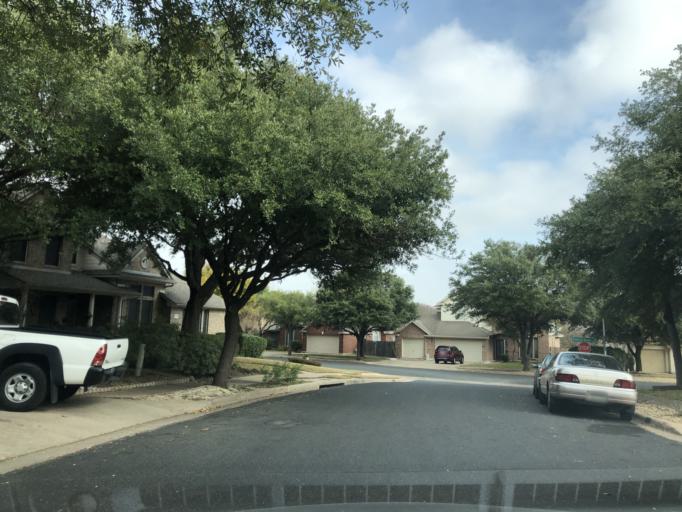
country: US
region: Texas
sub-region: Travis County
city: Wells Branch
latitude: 30.4189
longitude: -97.6835
